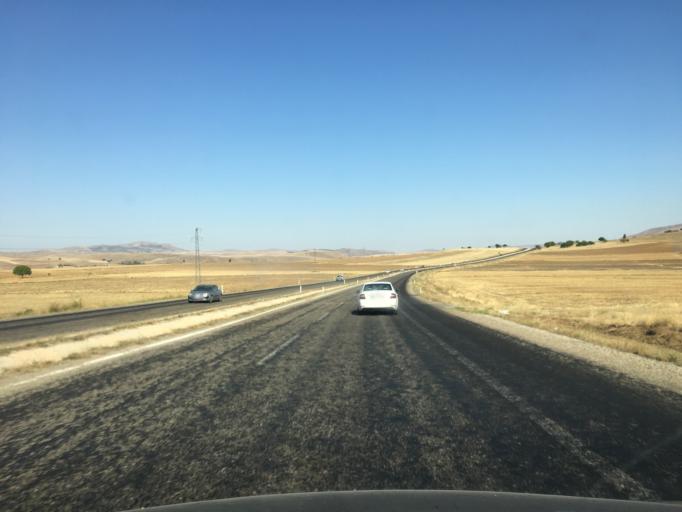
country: TR
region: Kirsehir
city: Akpinar
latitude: 39.3602
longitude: 33.9142
